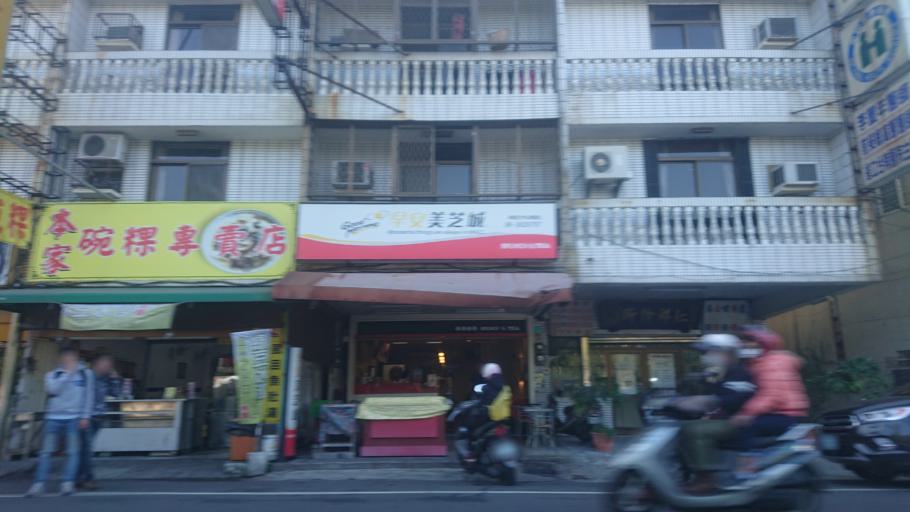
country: TW
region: Taiwan
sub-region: Tainan
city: Tainan
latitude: 23.0185
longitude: 120.2405
